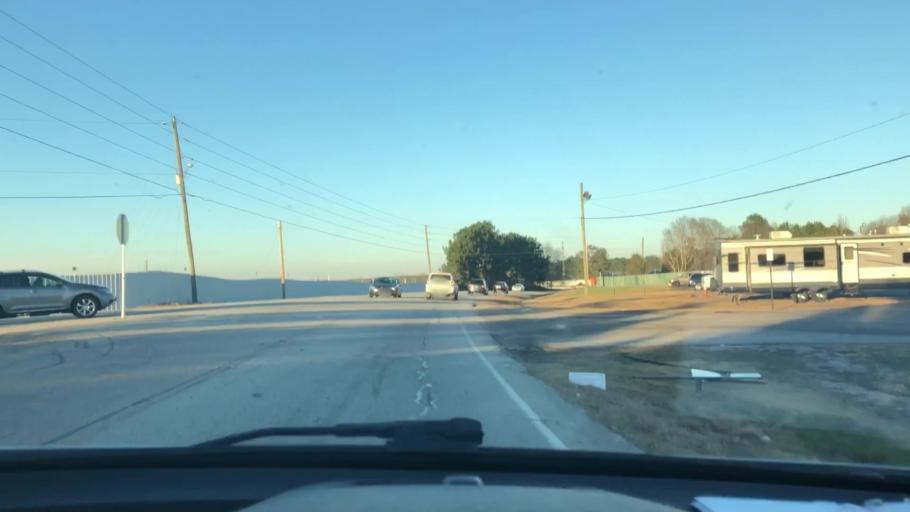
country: US
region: Georgia
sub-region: Walton County
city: Loganville
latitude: 33.8013
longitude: -83.9553
